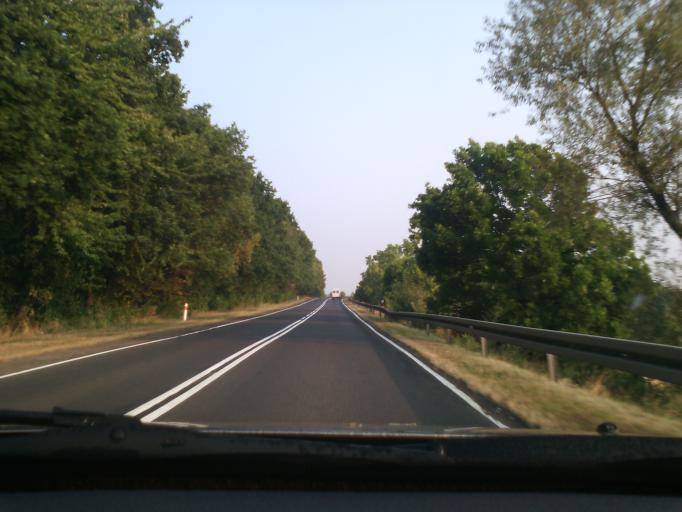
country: PL
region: Lower Silesian Voivodeship
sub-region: Powiat walbrzyski
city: Stare Bogaczowice
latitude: 50.9030
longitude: 16.2539
